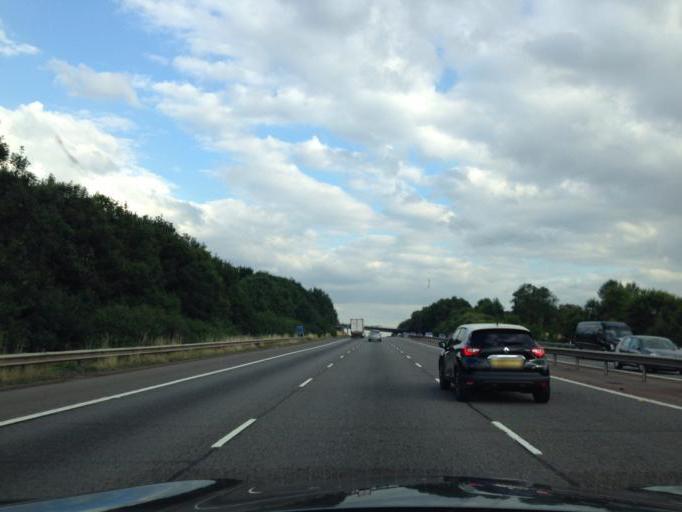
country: GB
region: England
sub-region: Oxfordshire
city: Hanwell
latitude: 52.0922
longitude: -1.3412
